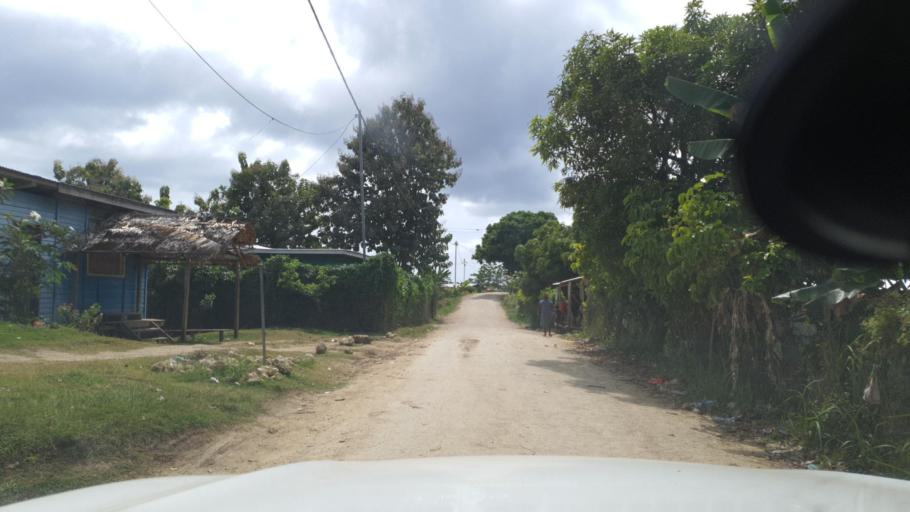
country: SB
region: Guadalcanal
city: Honiara
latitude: -9.4288
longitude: 159.9298
